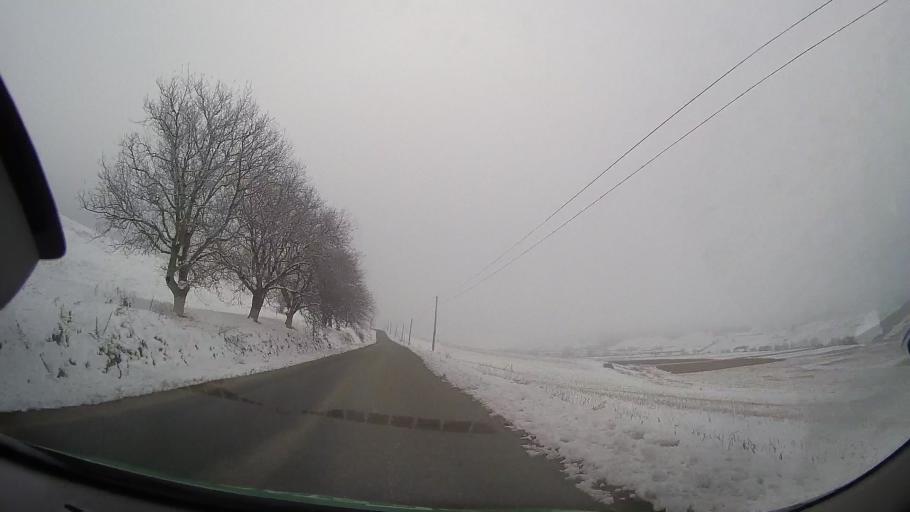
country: RO
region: Bacau
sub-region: Comuna Stanisesti
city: Stanisesti
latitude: 46.4144
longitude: 27.2691
